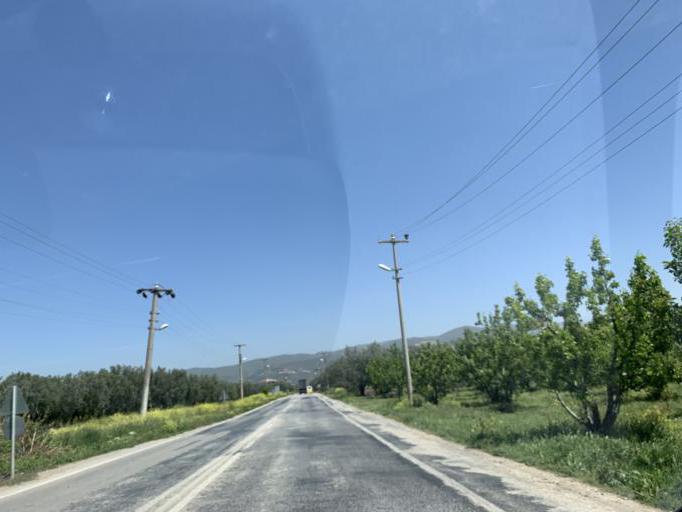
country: TR
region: Bursa
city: Iznik
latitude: 40.4128
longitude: 29.7100
